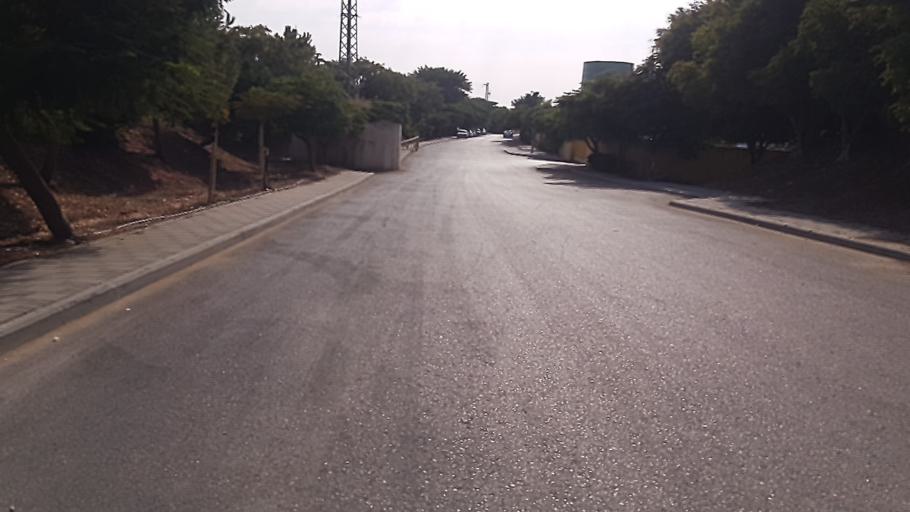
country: IL
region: Central District
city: Rosh Ha'Ayin
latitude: 32.0799
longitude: 34.9415
